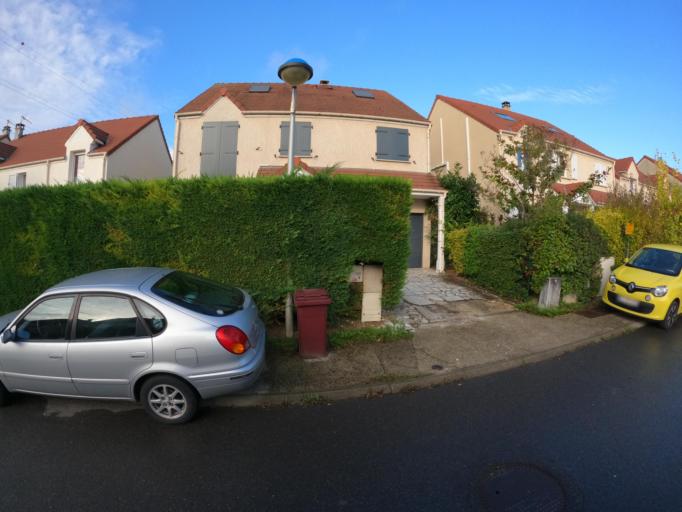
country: FR
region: Ile-de-France
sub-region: Departement de Seine-et-Marne
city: Brou-sur-Chantereine
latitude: 48.8894
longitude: 2.6246
